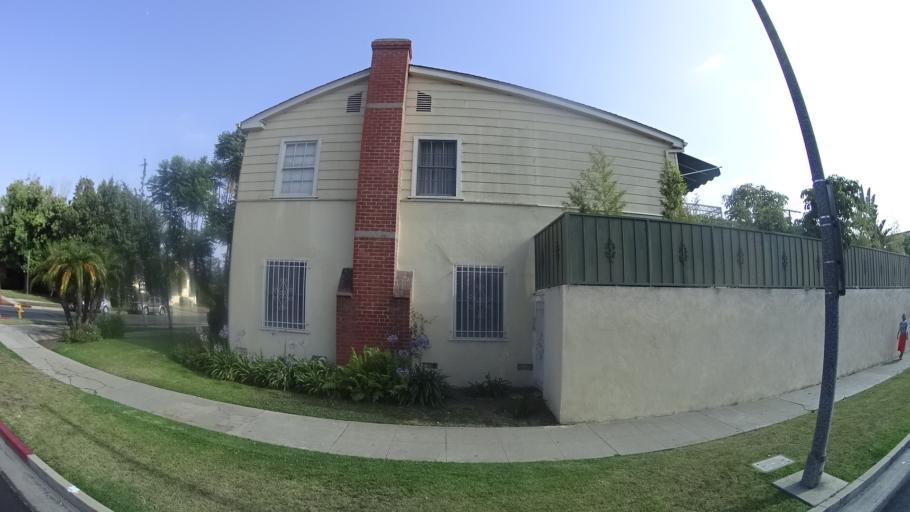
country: US
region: California
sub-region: Los Angeles County
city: West Hollywood
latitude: 34.0782
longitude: -118.3489
